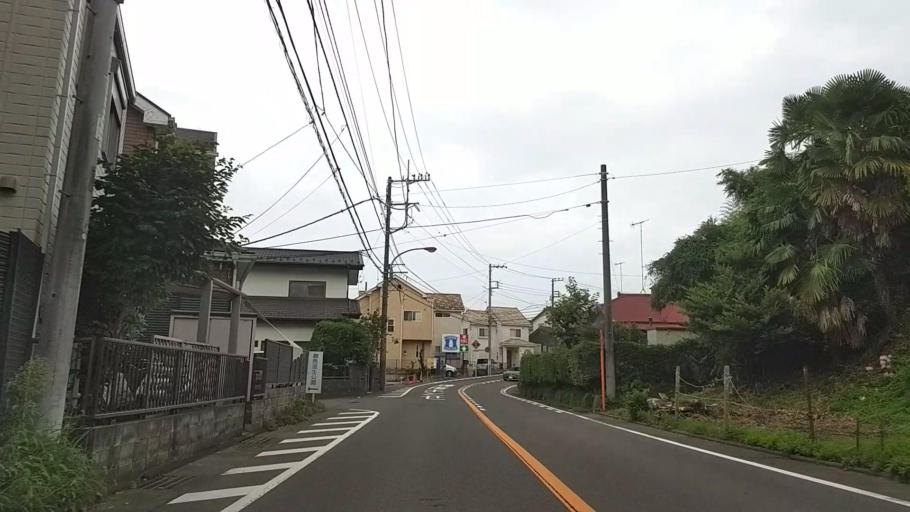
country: JP
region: Kanagawa
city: Hadano
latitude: 35.3394
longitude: 139.2345
